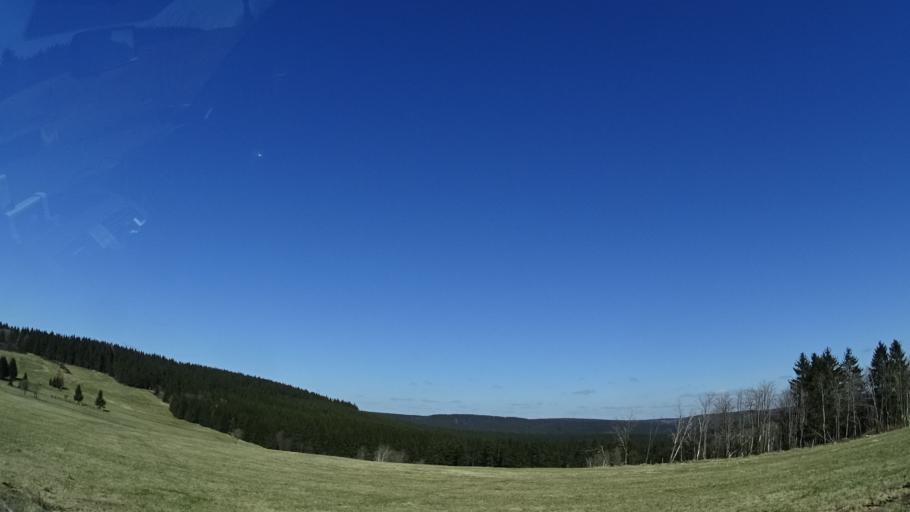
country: DE
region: Thuringia
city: Steinheid
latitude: 50.4594
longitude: 11.0931
